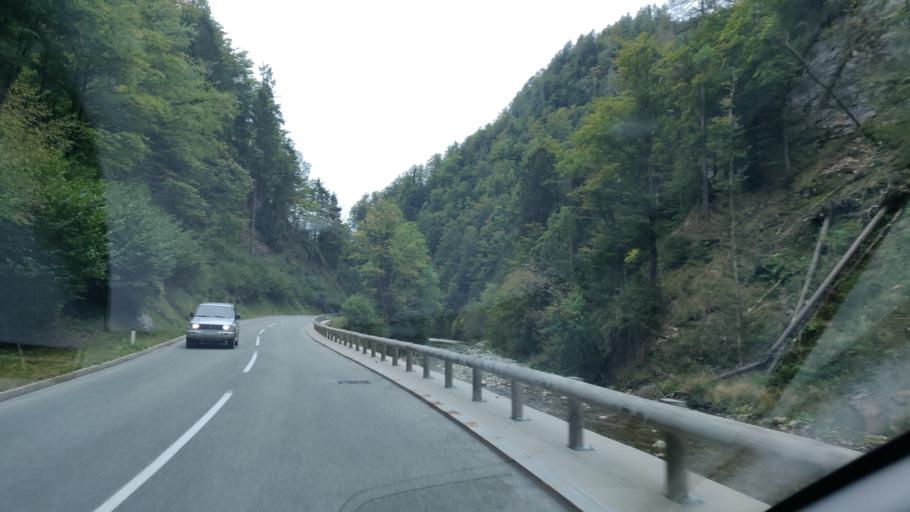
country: SI
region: Jezersko
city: Zgornje Jezersko
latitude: 46.3672
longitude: 14.4671
